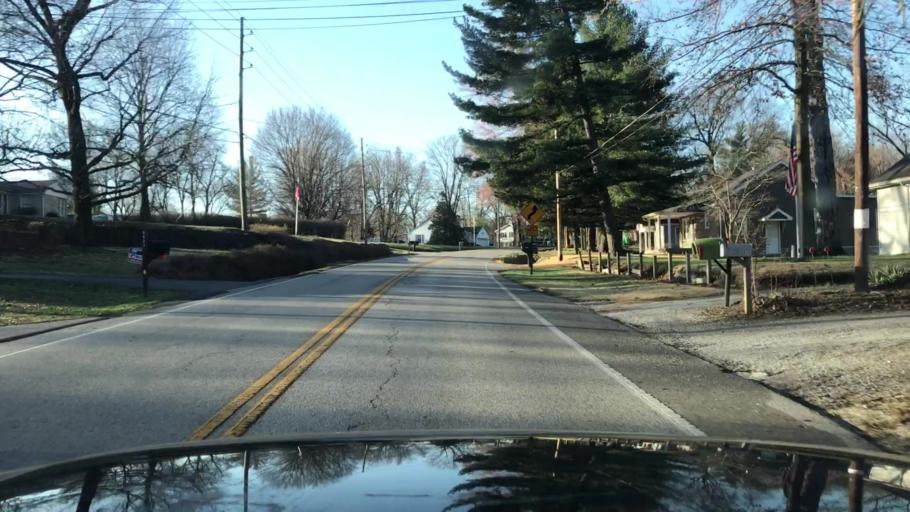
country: US
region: Indiana
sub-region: Vanderburgh County
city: Highland
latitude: 38.0393
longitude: -87.5620
